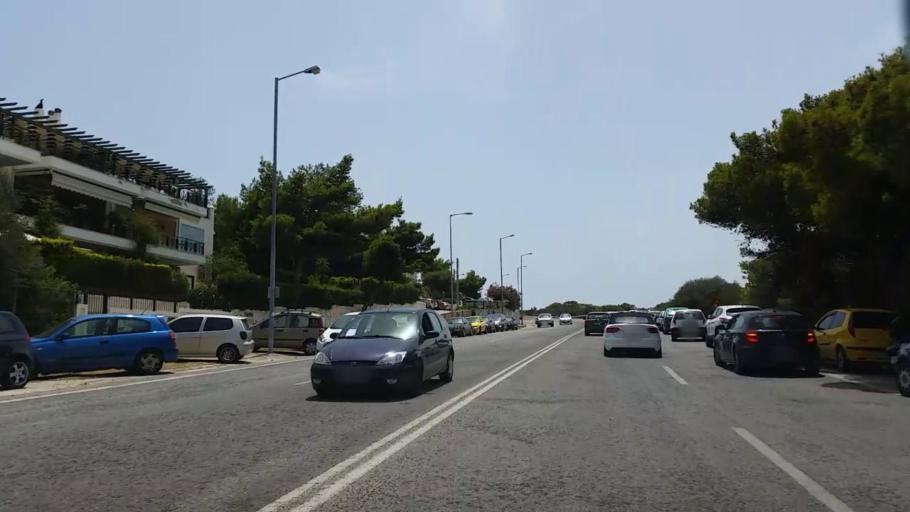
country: GR
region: Attica
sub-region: Nomarchia Anatolikis Attikis
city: Saronida
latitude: 37.7474
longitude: 23.9049
